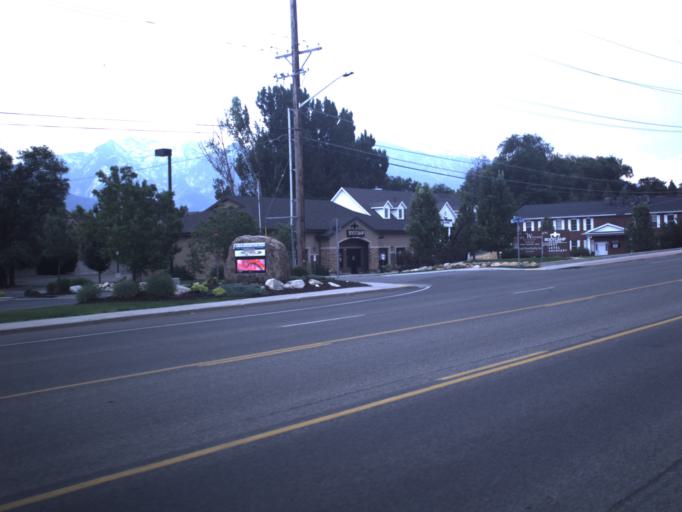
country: US
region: Utah
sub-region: Salt Lake County
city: Midvale
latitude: 40.6293
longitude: -111.8661
